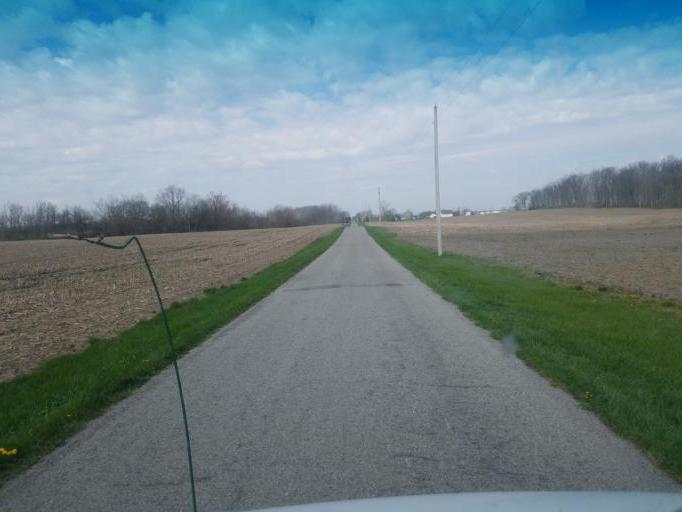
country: US
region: Ohio
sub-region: Logan County
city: Northwood
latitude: 40.4920
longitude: -83.7224
